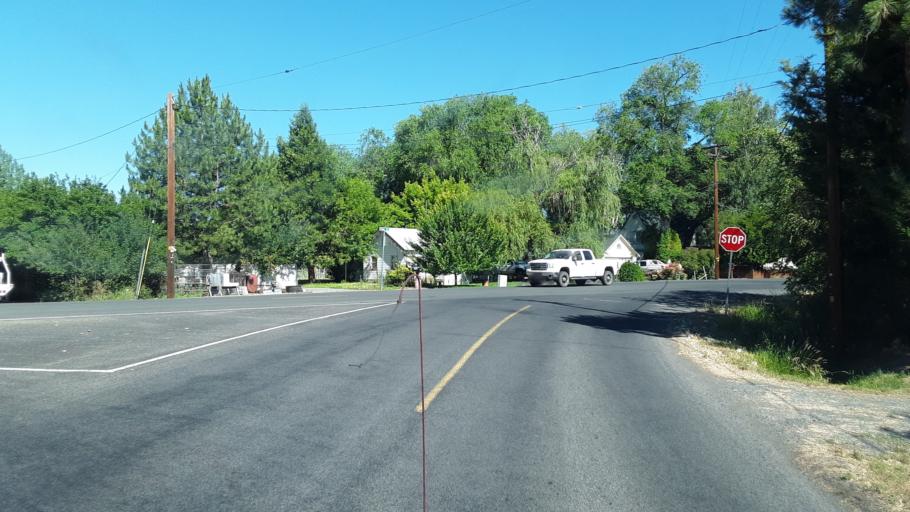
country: US
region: Oregon
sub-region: Klamath County
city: Altamont
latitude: 42.1987
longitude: -121.7298
